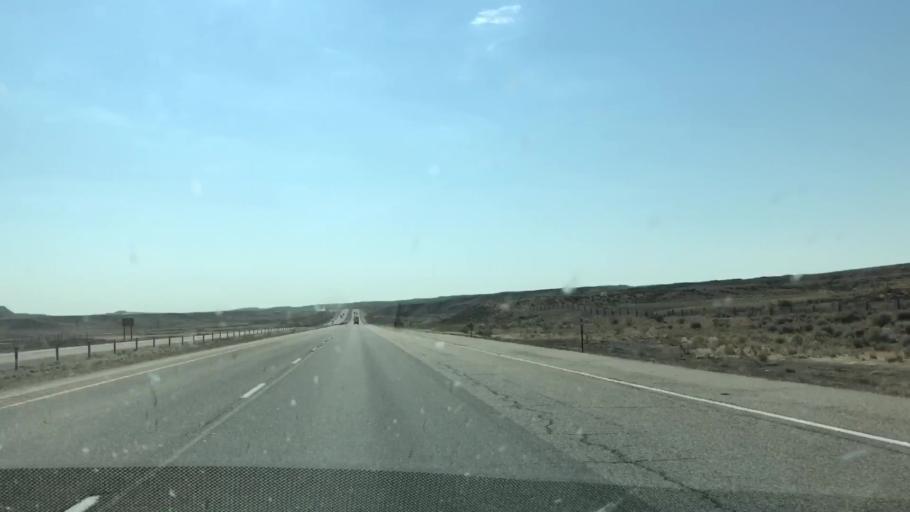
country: US
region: Wyoming
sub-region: Sweetwater County
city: Rock Springs
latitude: 41.6670
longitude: -108.7299
